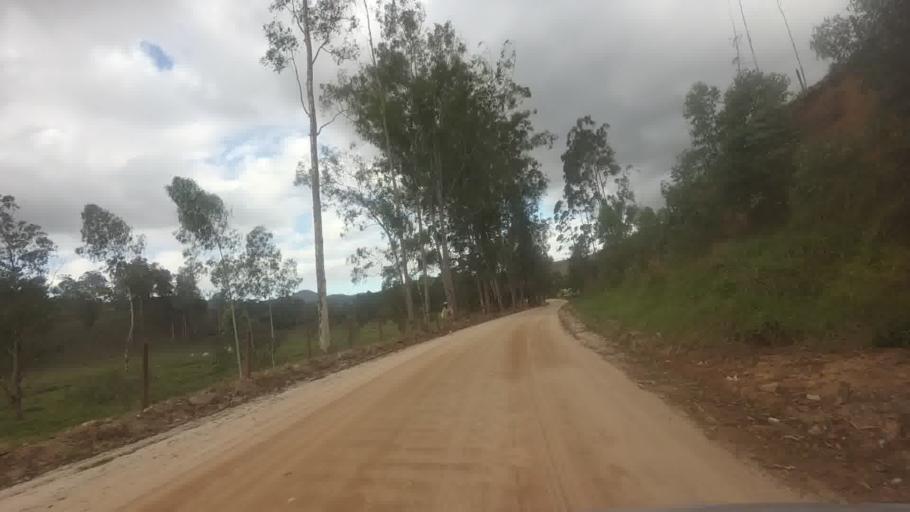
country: BR
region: Espirito Santo
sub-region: Mimoso Do Sul
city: Mimoso do Sul
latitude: -20.9521
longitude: -41.4243
